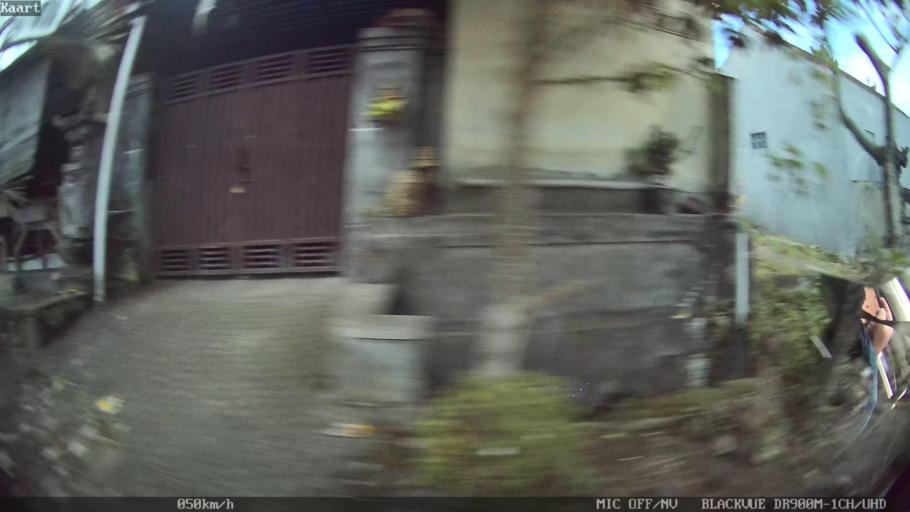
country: ID
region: Bali
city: Banjar Kelodan
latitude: -8.4777
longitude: 115.3746
